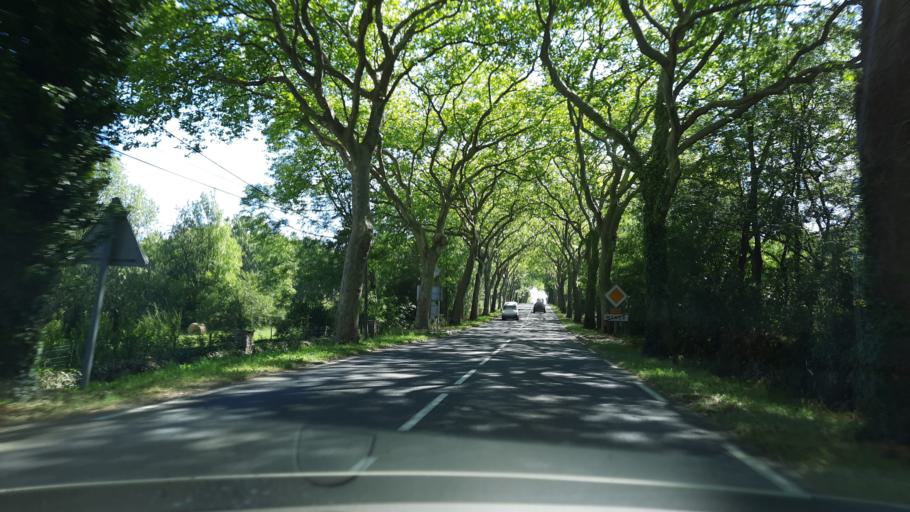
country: FR
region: Midi-Pyrenees
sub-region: Departement de l'Aveyron
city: Villefranche-de-Rouergue
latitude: 44.3235
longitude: 1.8988
